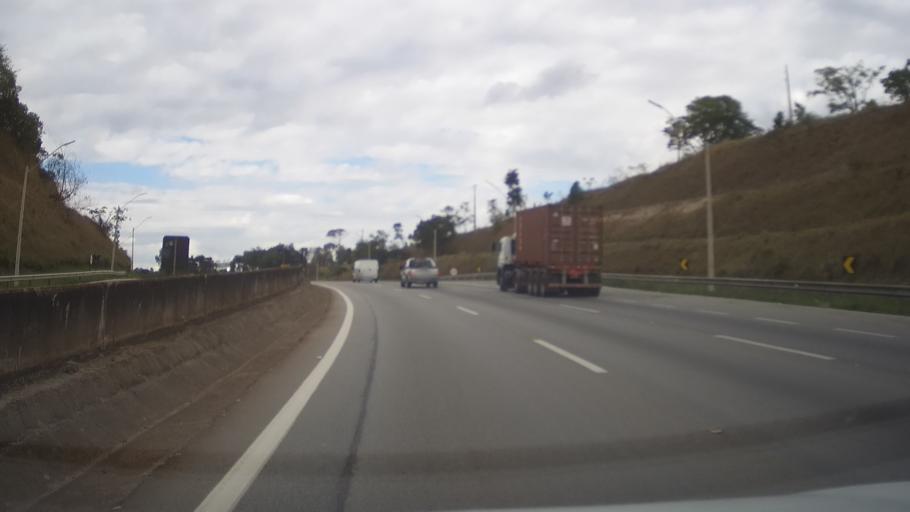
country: BR
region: Minas Gerais
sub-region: Itauna
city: Itauna
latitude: -20.3458
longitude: -44.4416
